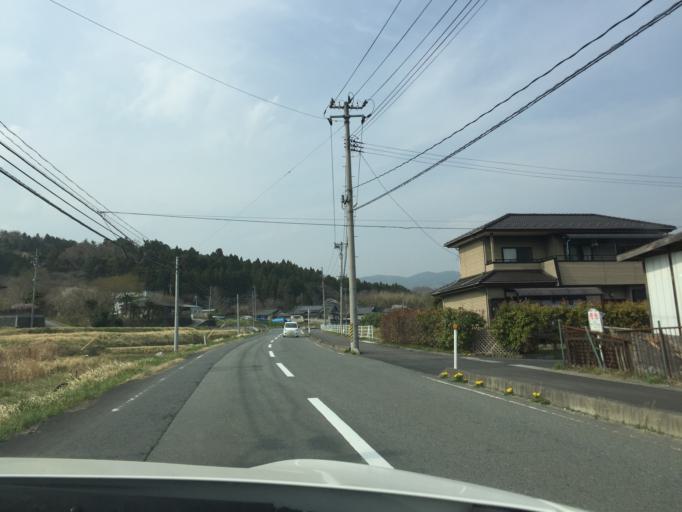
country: JP
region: Fukushima
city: Iwaki
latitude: 37.0103
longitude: 140.7366
